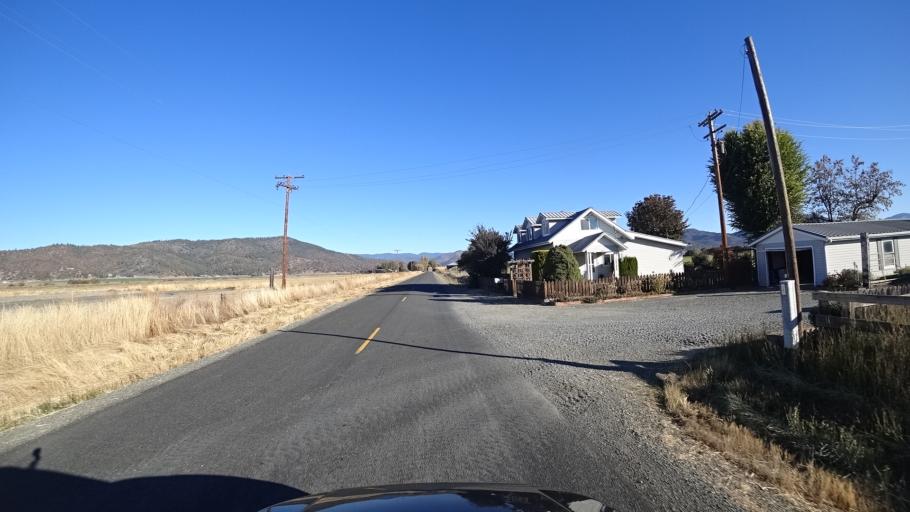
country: US
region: California
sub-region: Siskiyou County
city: Yreka
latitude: 41.5592
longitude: -122.8534
